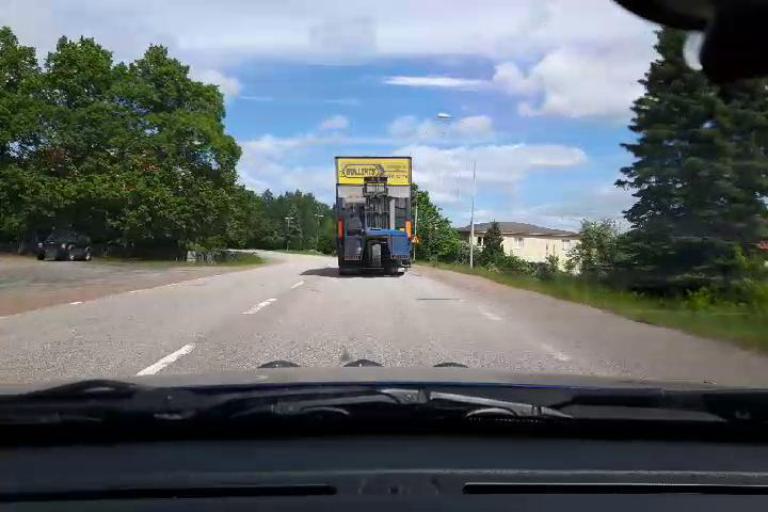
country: SE
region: Uppsala
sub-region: Osthammars Kommun
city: Bjorklinge
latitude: 60.0885
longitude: 17.5535
